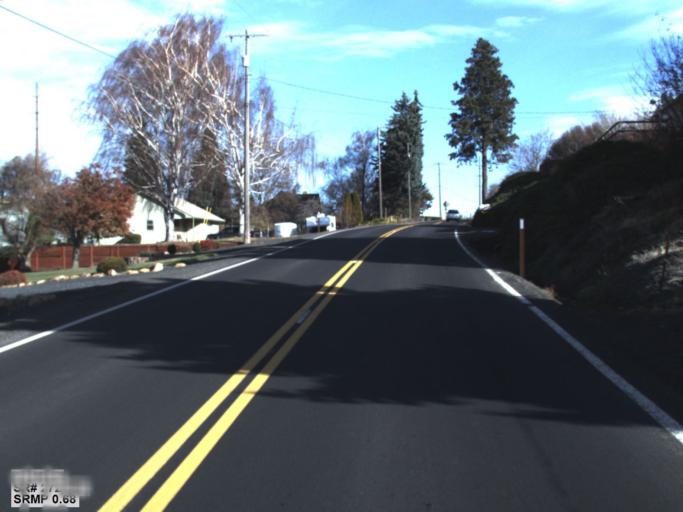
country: US
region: Washington
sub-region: Whitman County
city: Colfax
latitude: 46.8839
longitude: -117.3521
